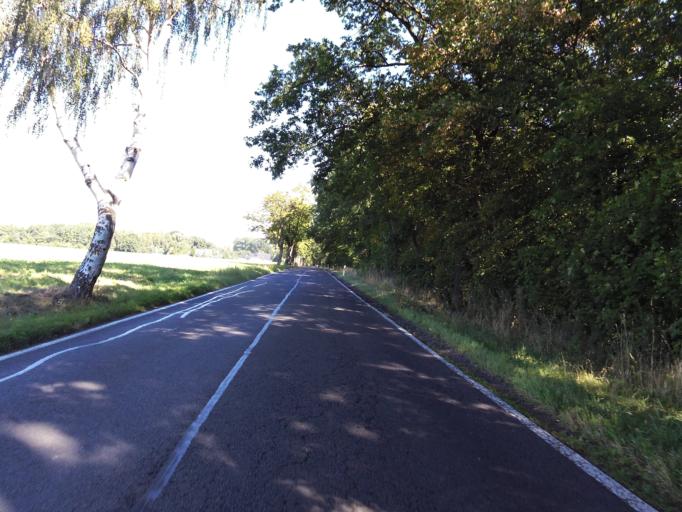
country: DE
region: Saxony-Anhalt
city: Pretzsch
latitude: 51.6812
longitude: 12.8268
